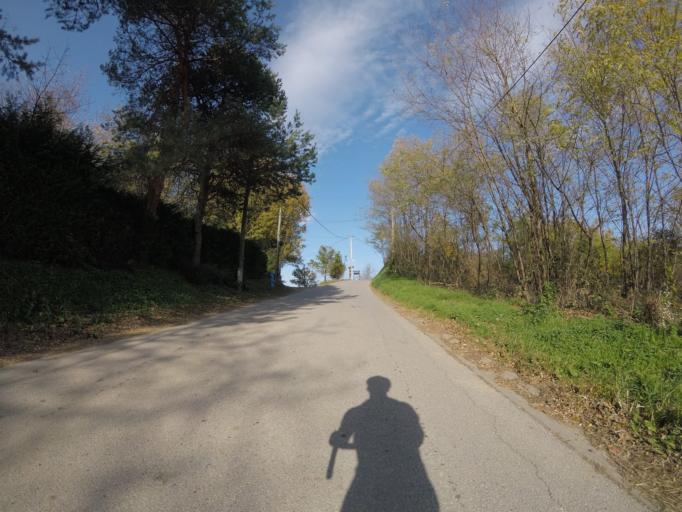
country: HR
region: Zagrebacka
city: Lukavec
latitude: 45.6111
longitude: 16.0027
